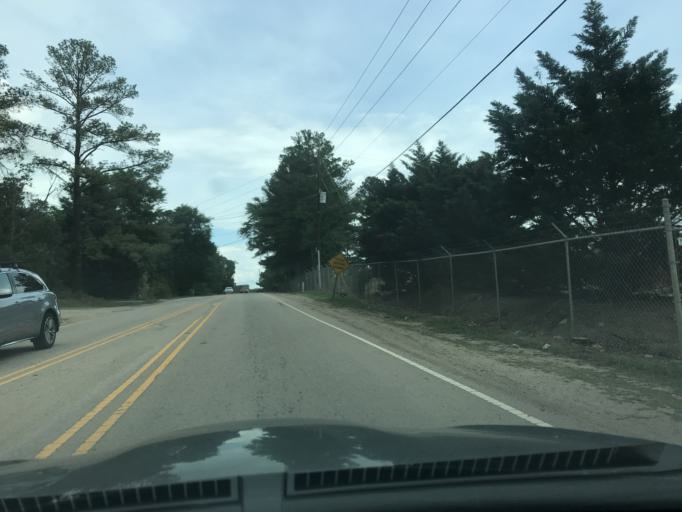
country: US
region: North Carolina
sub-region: Wake County
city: Raleigh
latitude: 35.8842
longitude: -78.5877
